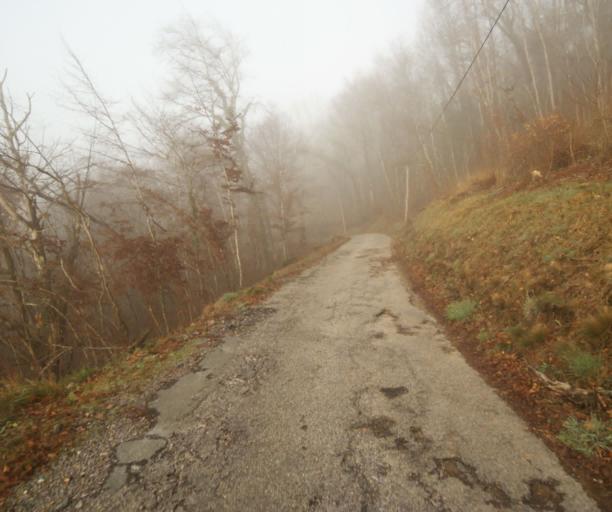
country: FR
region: Limousin
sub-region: Departement de la Correze
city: Laguenne
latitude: 45.2618
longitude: 1.7864
